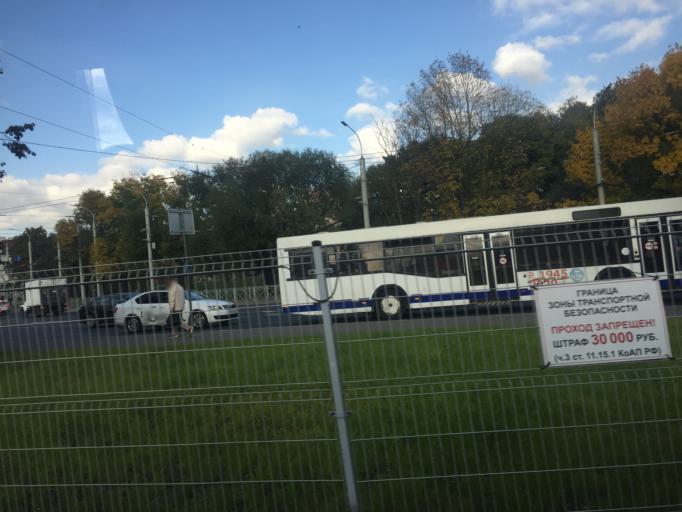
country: RU
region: Kaliningrad
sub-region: Gorod Kaliningrad
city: Kaliningrad
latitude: 54.6936
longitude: 20.5029
